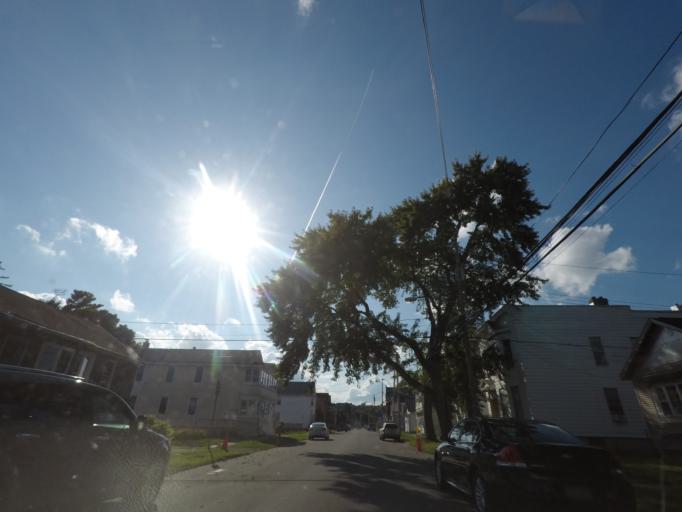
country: US
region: New York
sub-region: Albany County
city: Watervliet
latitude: 42.7345
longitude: -73.7065
